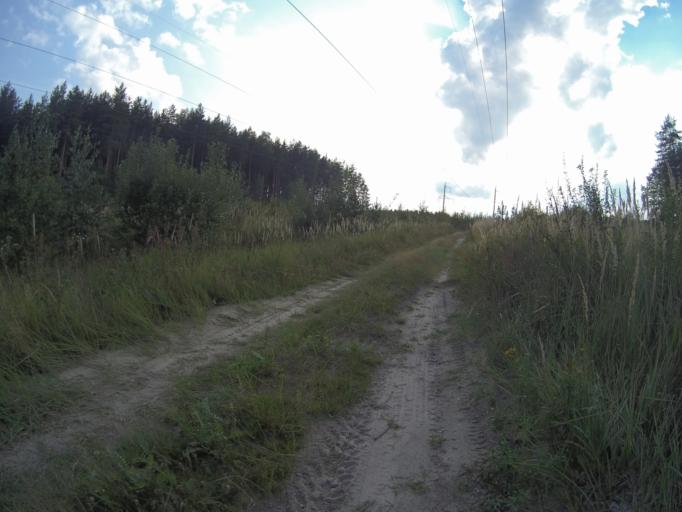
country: RU
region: Vladimir
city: Raduzhnyy
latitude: 56.0151
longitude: 40.2955
